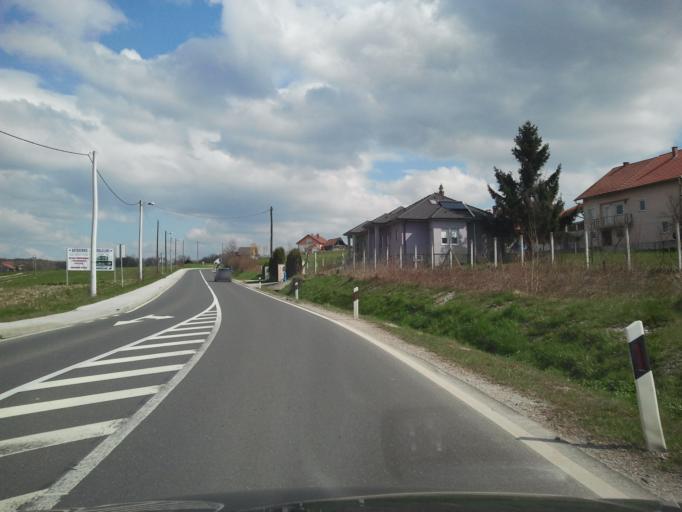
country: HR
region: Grad Zagreb
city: Horvati
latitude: 45.6934
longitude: 15.7482
